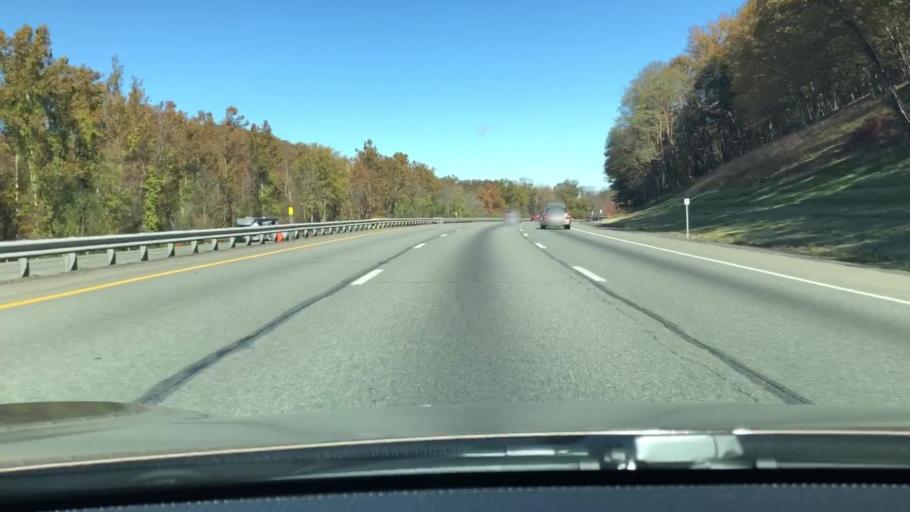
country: US
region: New York
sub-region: Rockland County
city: Sloatsburg
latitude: 41.2253
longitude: -74.1836
